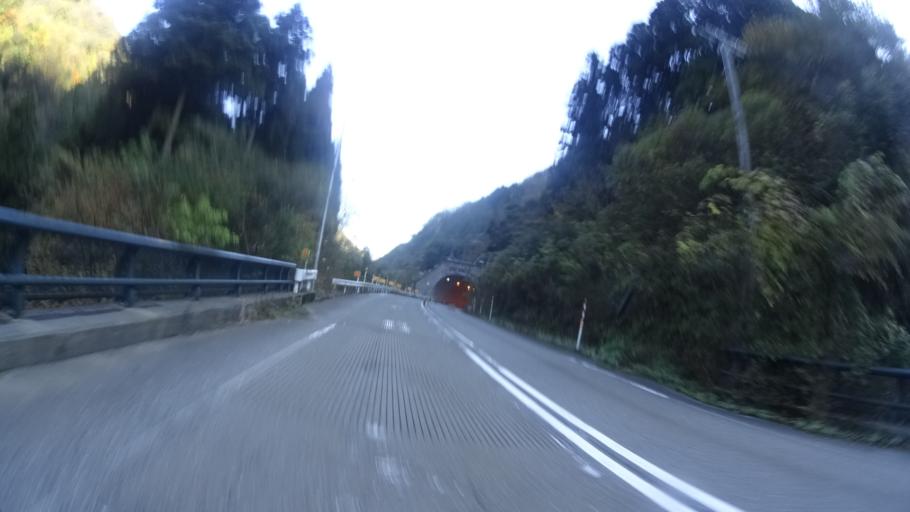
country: JP
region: Fukui
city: Maruoka
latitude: 36.1945
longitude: 136.3447
